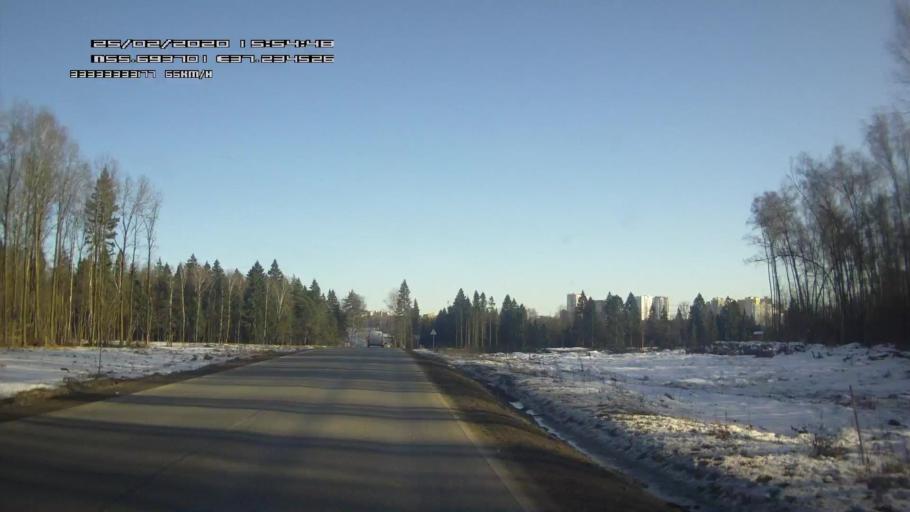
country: RU
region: Moskovskaya
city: Odintsovo
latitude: 55.6938
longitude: 37.2345
